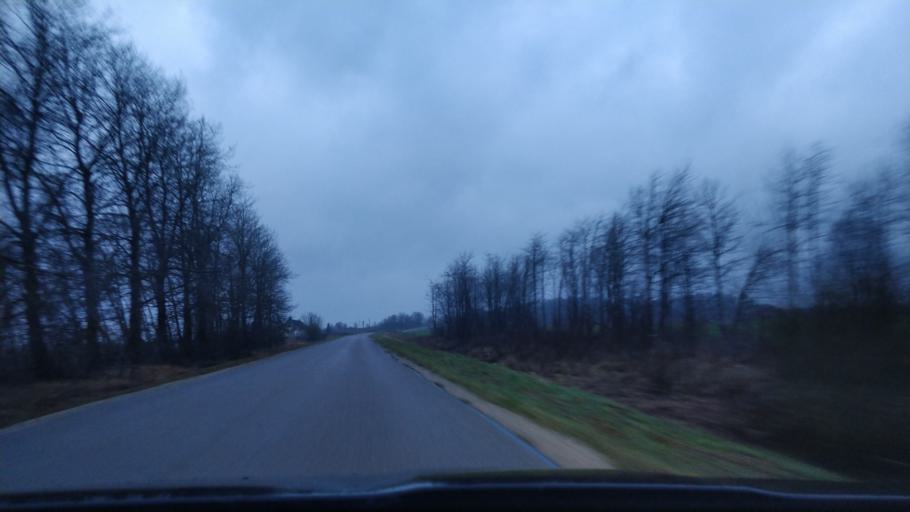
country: EE
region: Laeaene
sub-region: Lihula vald
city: Lihula
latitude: 58.6980
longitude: 23.8533
